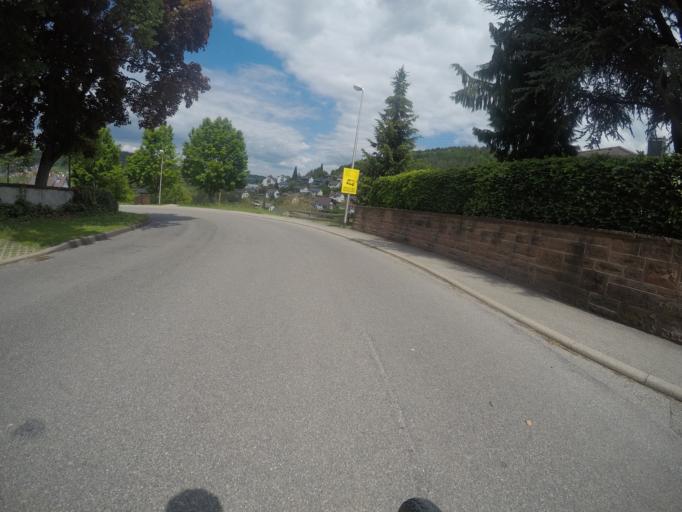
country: DE
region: Baden-Wuerttemberg
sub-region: Karlsruhe Region
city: Nagold
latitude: 48.5848
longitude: 8.7380
